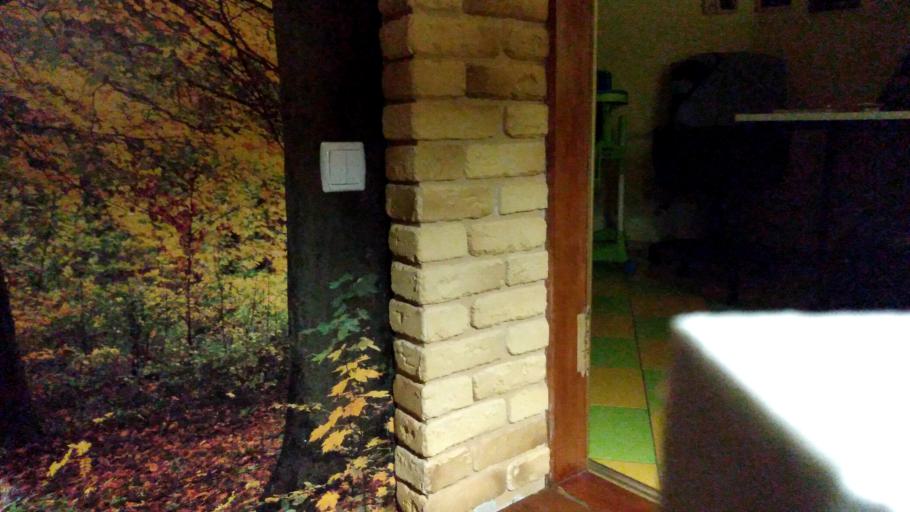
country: RU
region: Vologda
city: Lipin Bor
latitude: 60.8491
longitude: 38.0154
